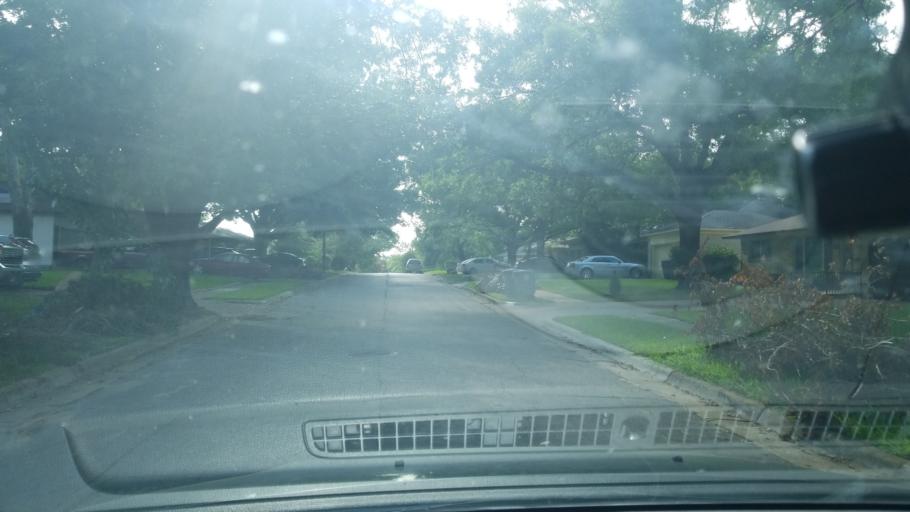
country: US
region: Texas
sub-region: Dallas County
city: Balch Springs
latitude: 32.7419
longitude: -96.6679
